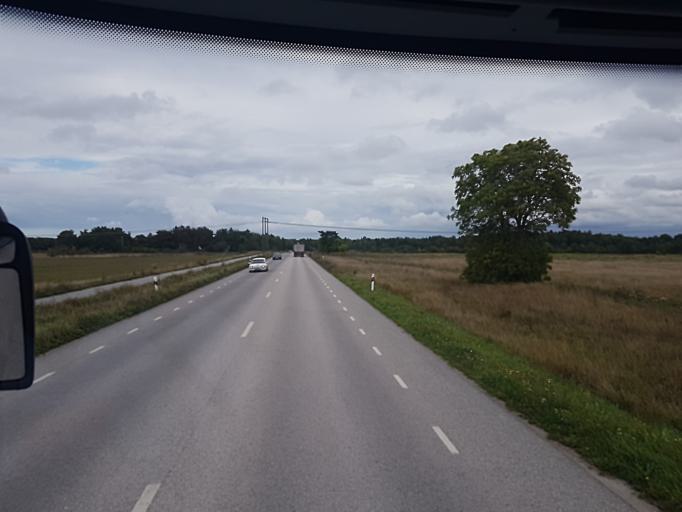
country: SE
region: Gotland
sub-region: Gotland
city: Vibble
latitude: 57.5776
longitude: 18.2109
